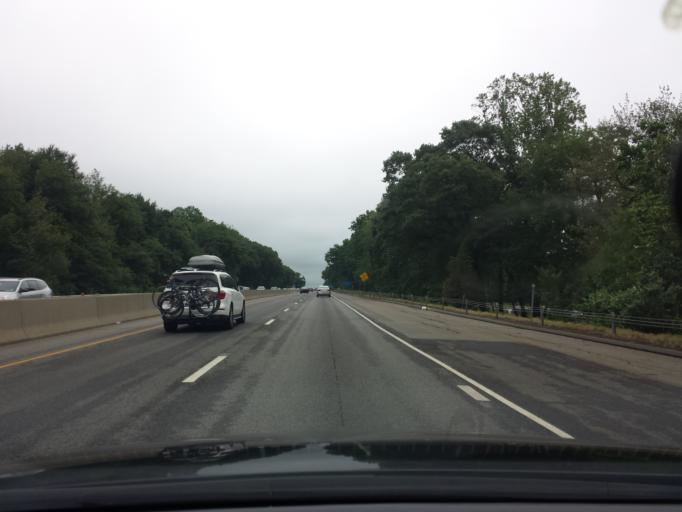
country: US
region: Connecticut
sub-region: Middlesex County
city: Westbrook Center
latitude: 41.2913
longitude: -72.4386
